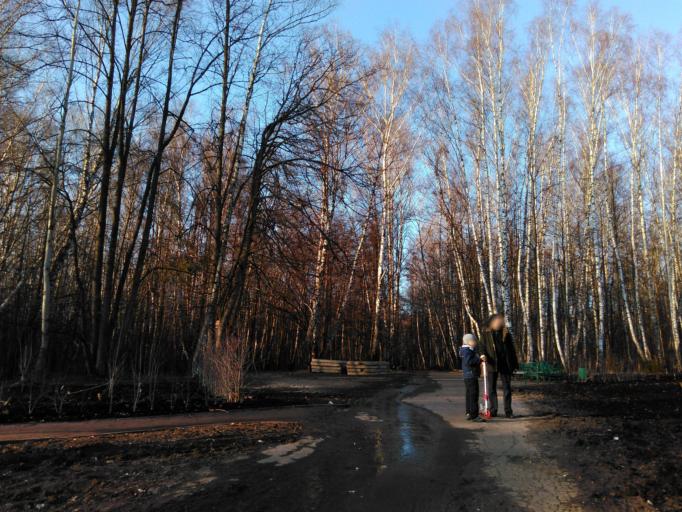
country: RU
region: Moscow
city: Zyuzino
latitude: 55.6388
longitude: 37.5643
